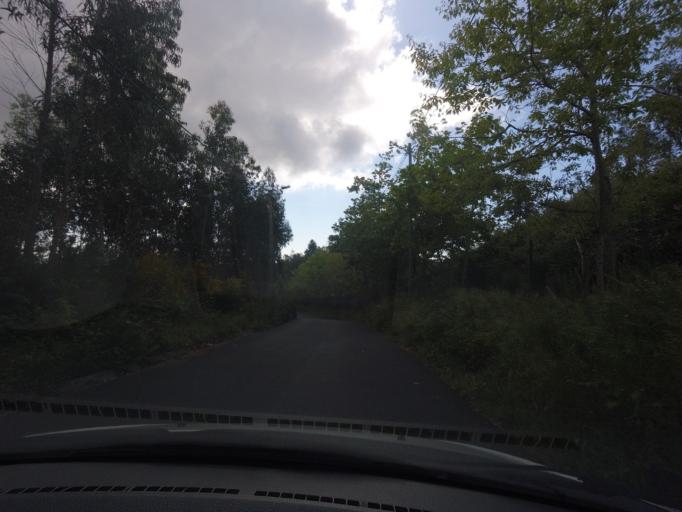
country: PT
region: Madeira
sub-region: Santa Cruz
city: Camacha
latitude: 32.6710
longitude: -16.8579
